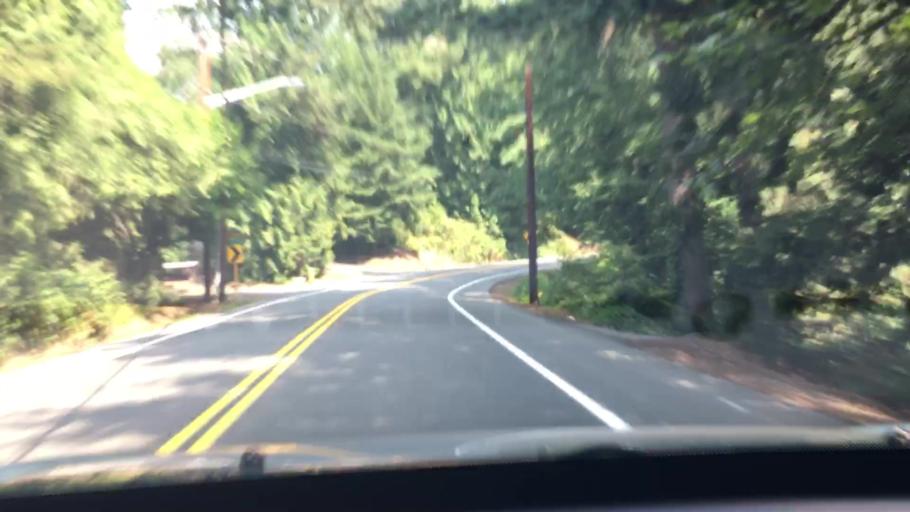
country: US
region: Washington
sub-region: King County
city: City of Sammamish
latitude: 47.6109
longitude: -122.0645
